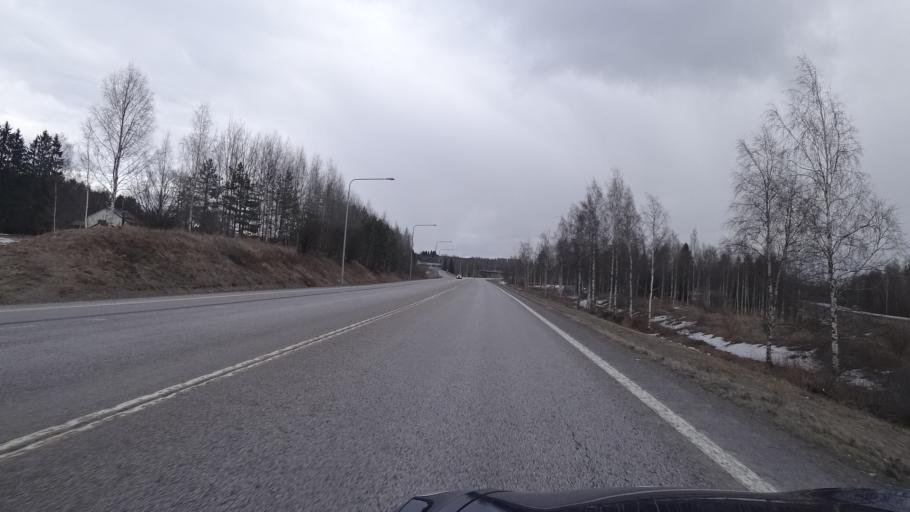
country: FI
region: Paijanne Tavastia
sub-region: Lahti
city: Nastola
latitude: 60.9462
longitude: 25.8746
